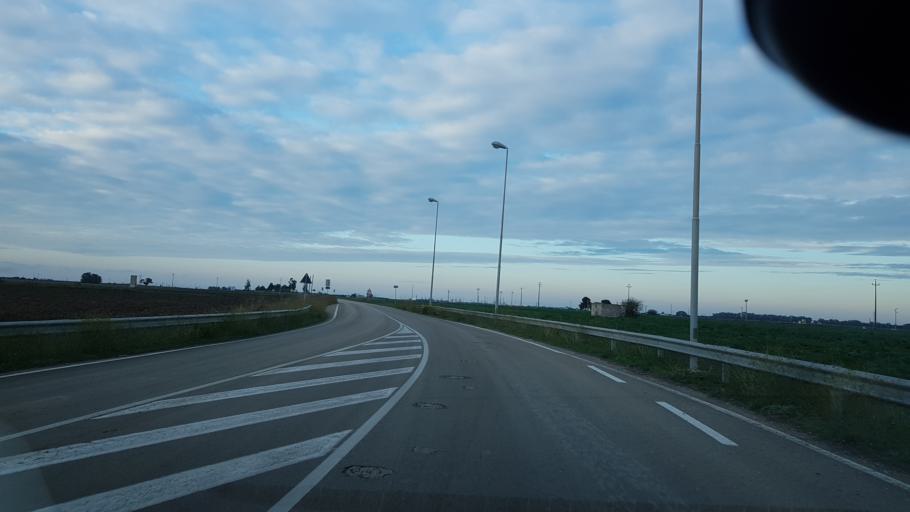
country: IT
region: Apulia
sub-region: Provincia di Brindisi
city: Tuturano
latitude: 40.5700
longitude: 18.0159
